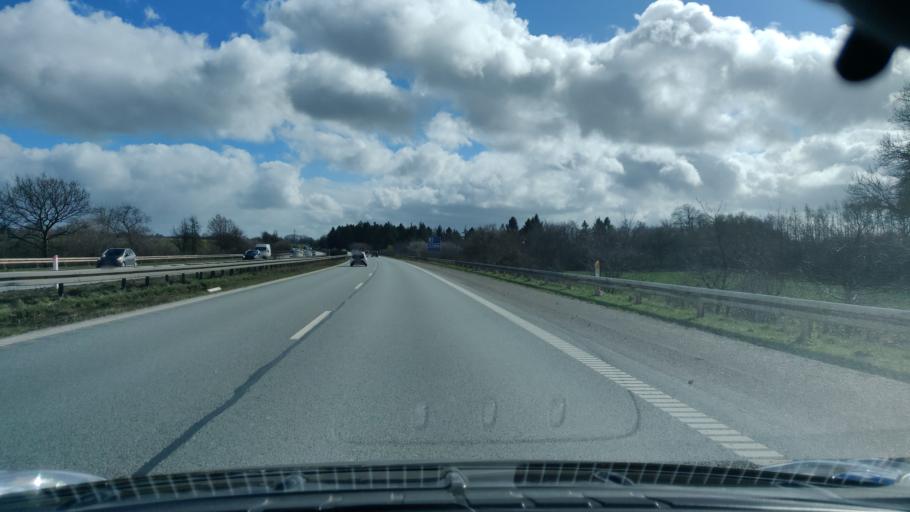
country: DK
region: Zealand
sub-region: Lejre Kommune
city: Lejre
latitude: 55.6298
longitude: 11.9656
